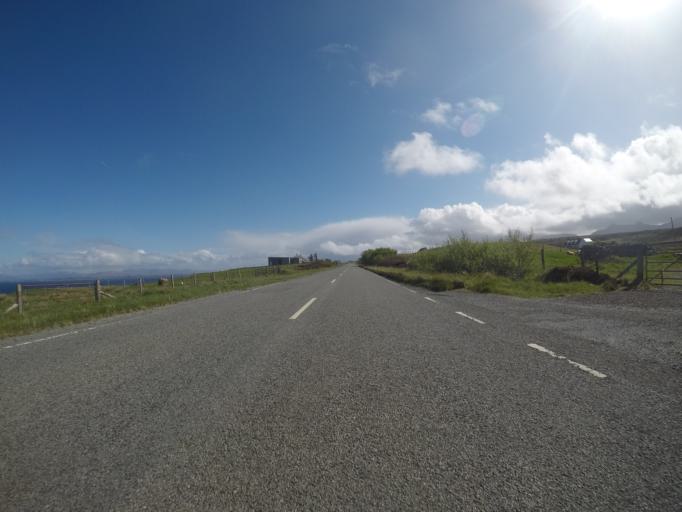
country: GB
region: Scotland
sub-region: Highland
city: Portree
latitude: 57.5984
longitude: -6.1630
